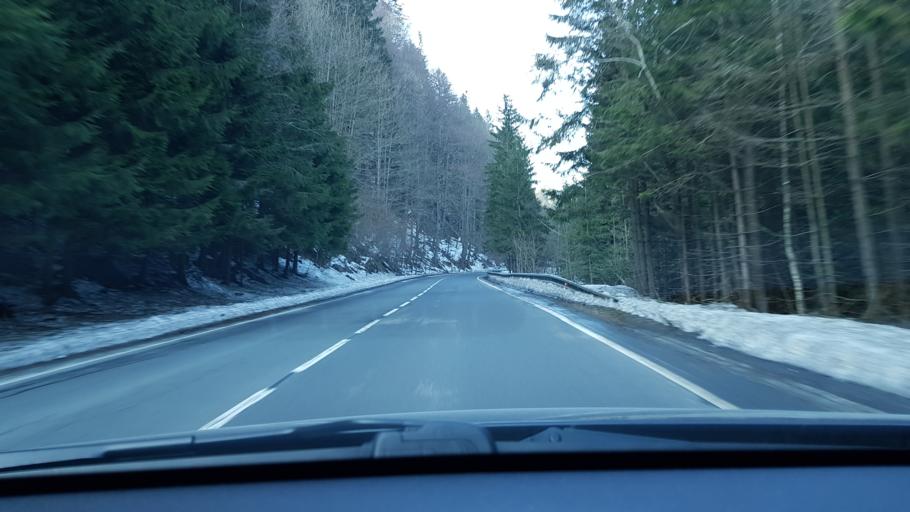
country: CZ
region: Olomoucky
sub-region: Okres Sumperk
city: Stare Mesto
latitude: 50.1388
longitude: 17.0123
